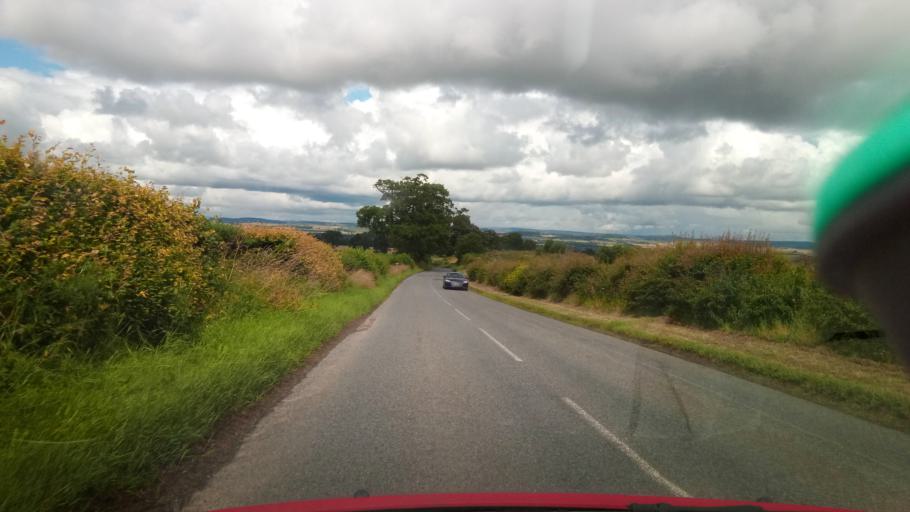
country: GB
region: Scotland
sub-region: The Scottish Borders
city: Kelso
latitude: 55.5668
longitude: -2.4163
